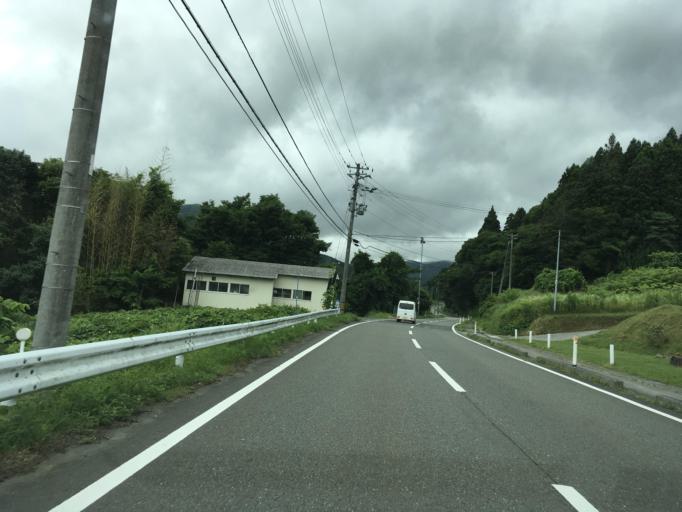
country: JP
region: Iwate
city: Ofunato
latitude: 38.8966
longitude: 141.4872
